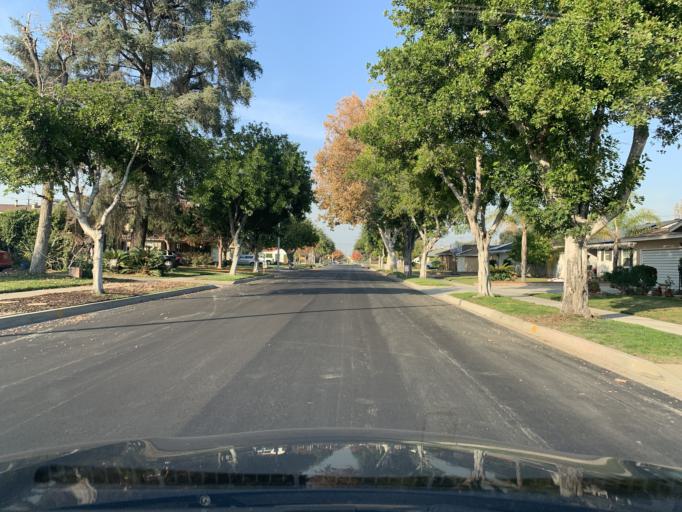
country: US
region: California
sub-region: Los Angeles County
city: Covina
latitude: 34.0878
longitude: -117.9020
